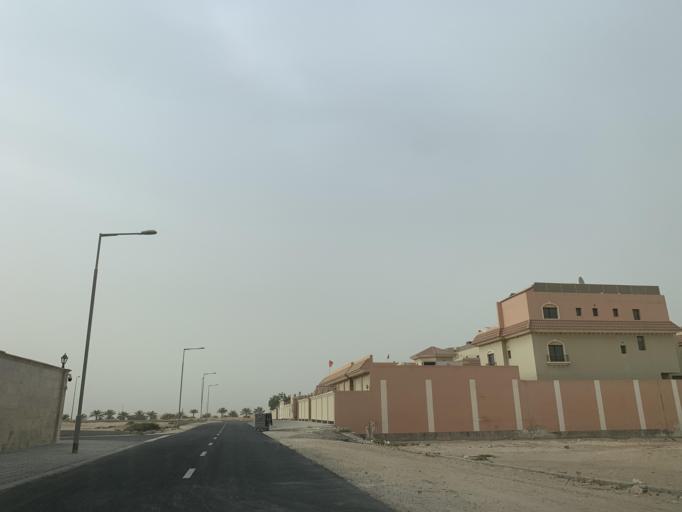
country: BH
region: Central Governorate
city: Madinat Hamad
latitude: 26.1399
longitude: 50.5245
